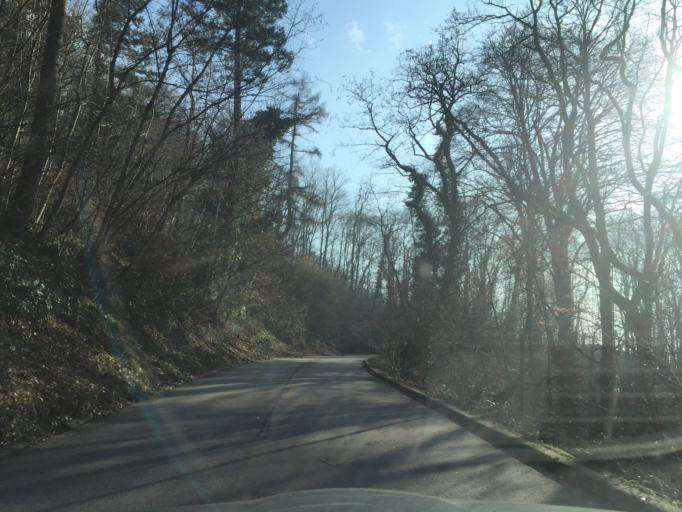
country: DE
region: Baden-Wuerttemberg
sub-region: Karlsruhe Region
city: Weinheim
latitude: 49.5502
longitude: 8.6829
